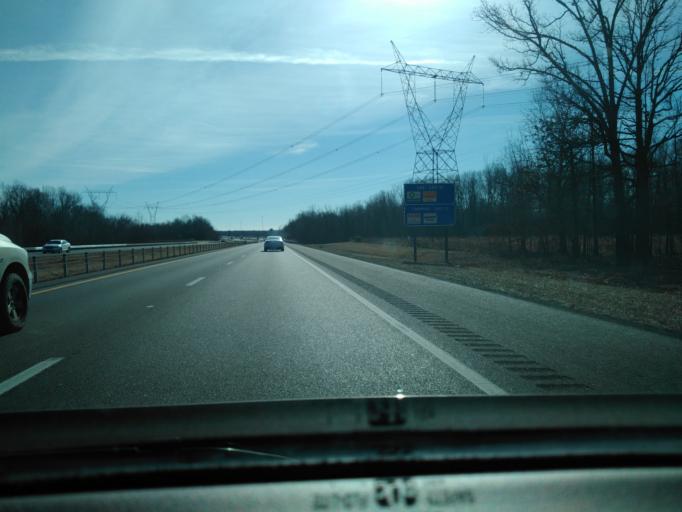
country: US
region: Kentucky
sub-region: McCracken County
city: Hendron
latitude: 37.0214
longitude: -88.6058
